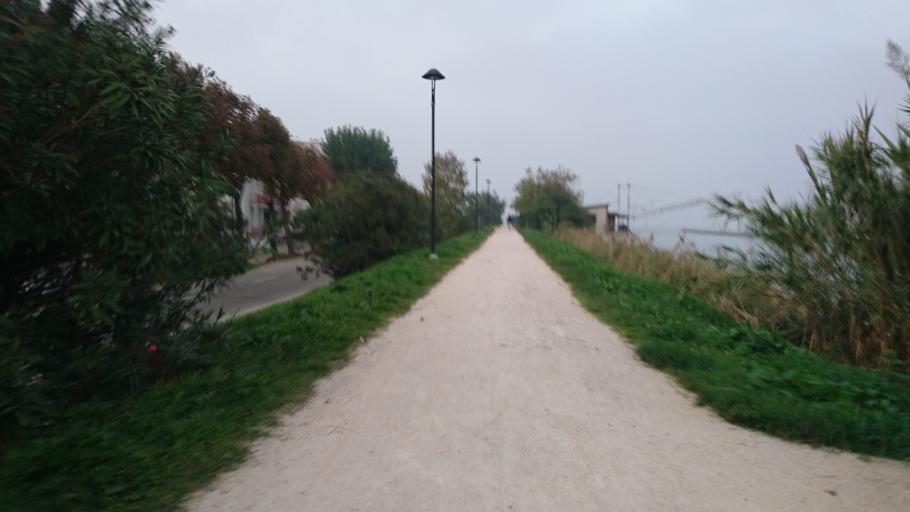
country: IT
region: Emilia-Romagna
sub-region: Provincia di Rimini
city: Rimini
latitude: 44.0744
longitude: 12.5610
